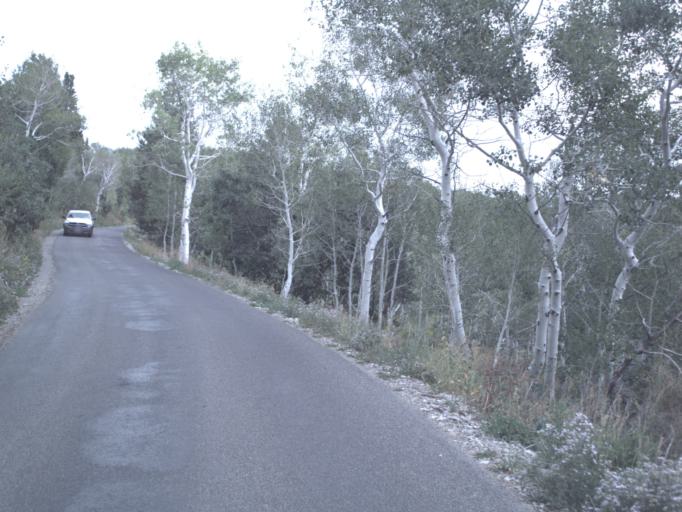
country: US
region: Utah
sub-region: Utah County
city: Lindon
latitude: 40.4362
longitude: -111.6171
